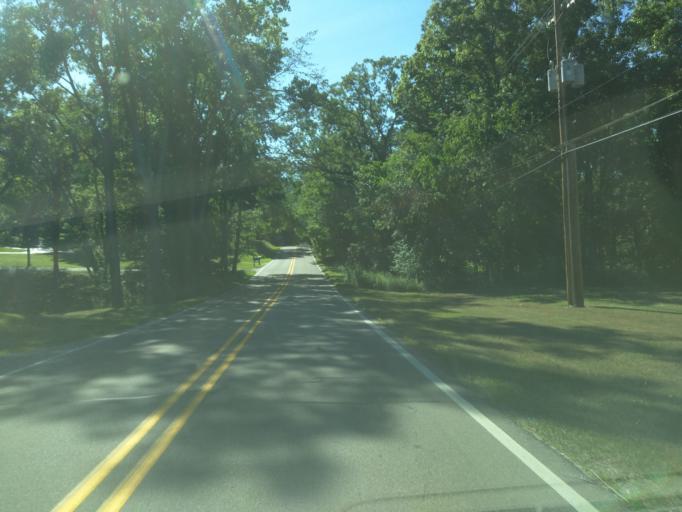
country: US
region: Michigan
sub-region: Eaton County
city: Waverly
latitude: 42.7646
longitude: -84.6177
